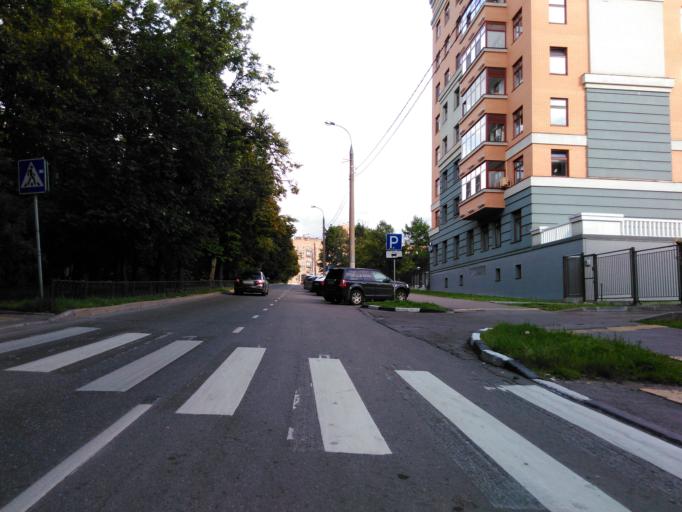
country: RU
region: Moskovskaya
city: Semenovskoye
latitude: 55.6817
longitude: 37.5304
